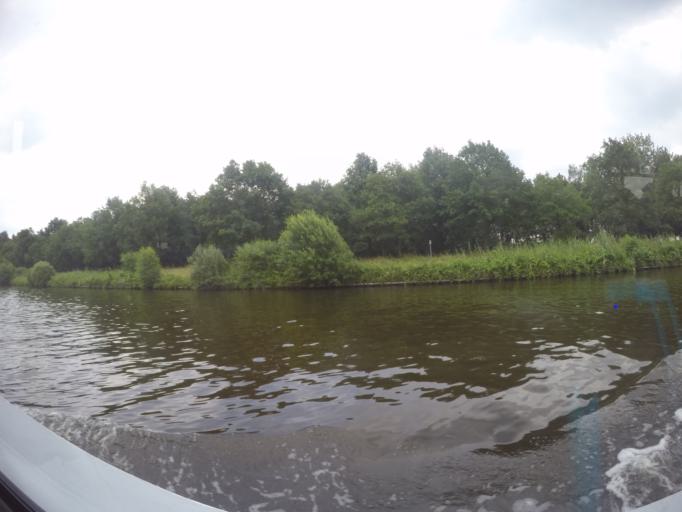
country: NL
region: Overijssel
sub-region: Gemeente Hof van Twente
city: Hengevelde
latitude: 52.2620
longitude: 6.6458
